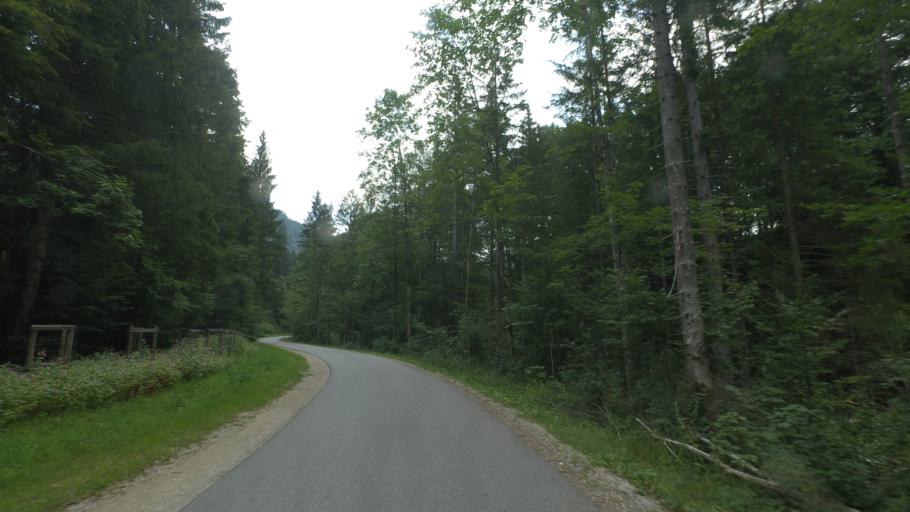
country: DE
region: Bavaria
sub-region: Upper Bavaria
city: Ruhpolding
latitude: 47.7351
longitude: 12.6006
